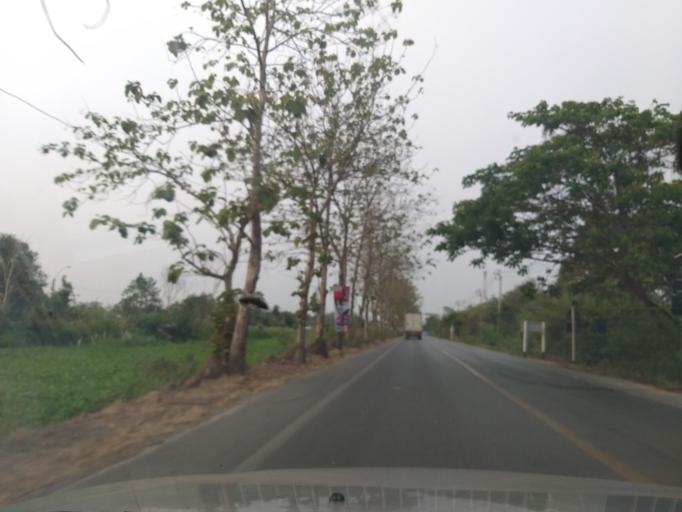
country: TH
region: Bangkok
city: Nong Chok
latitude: 13.9051
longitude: 100.8892
